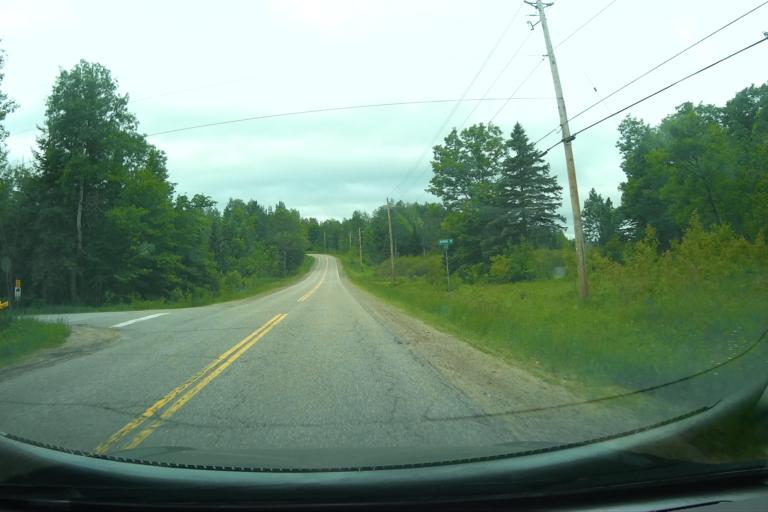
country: CA
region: Ontario
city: Pembroke
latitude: 45.4837
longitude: -77.2071
